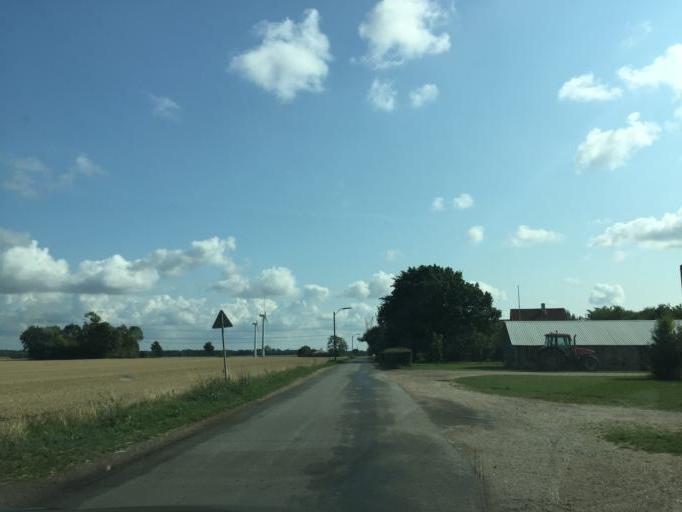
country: DK
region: South Denmark
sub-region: Odense Kommune
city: Bellinge
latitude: 55.3339
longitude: 10.3763
